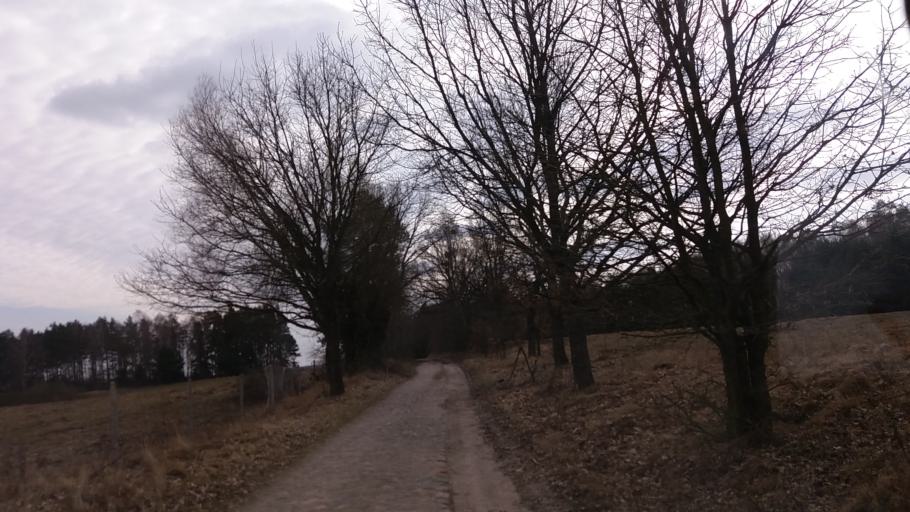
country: PL
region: West Pomeranian Voivodeship
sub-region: Powiat choszczenski
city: Bierzwnik
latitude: 53.1374
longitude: 15.6268
